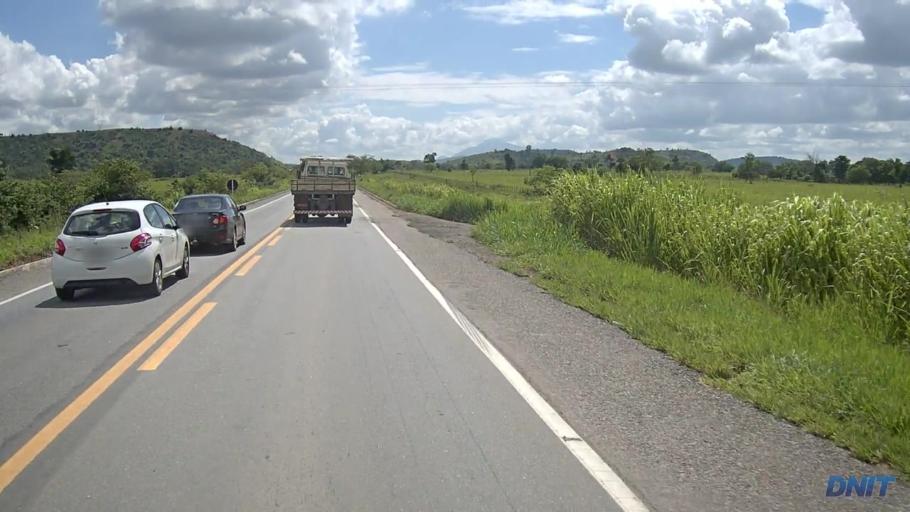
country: BR
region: Minas Gerais
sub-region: Governador Valadares
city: Governador Valadares
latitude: -19.0053
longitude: -42.1309
